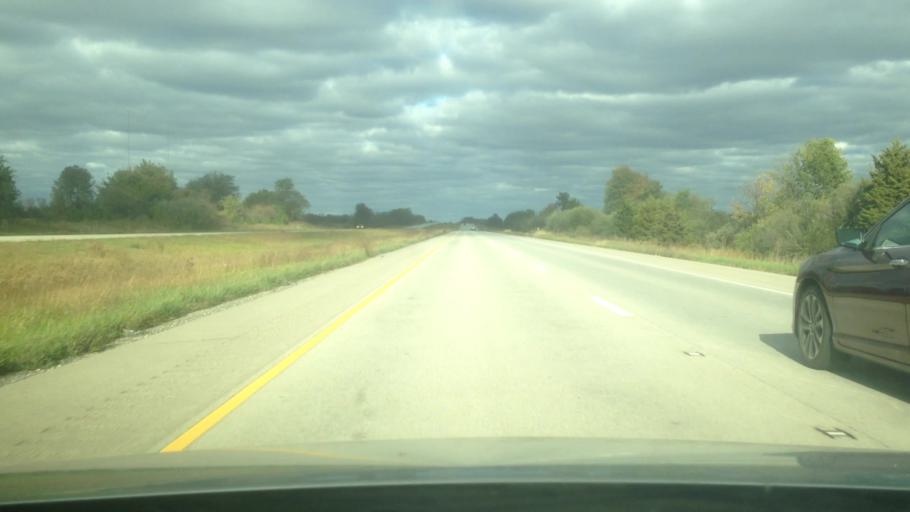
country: US
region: Illinois
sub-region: Macon County
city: Forsyth
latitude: 39.9203
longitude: -88.8582
